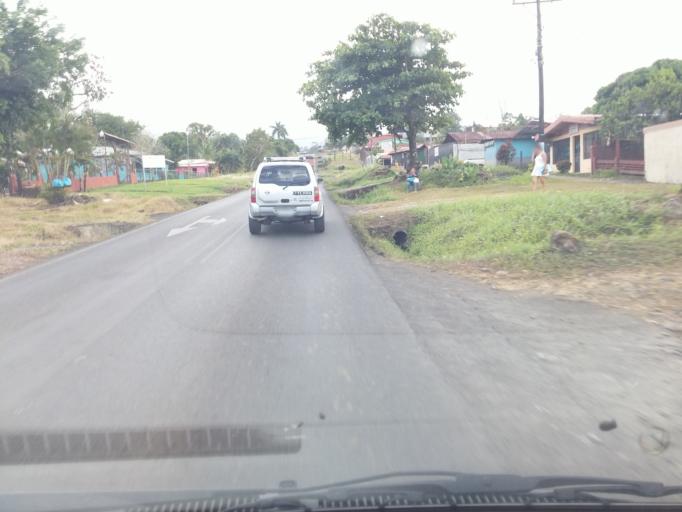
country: CR
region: Alajuela
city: Pital
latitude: 10.3907
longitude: -84.3387
